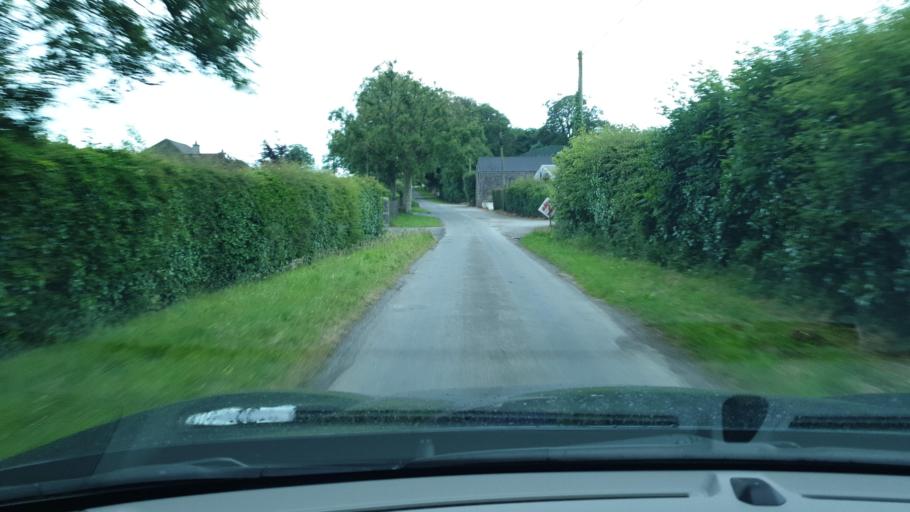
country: IE
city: Kentstown
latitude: 53.5919
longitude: -6.5693
